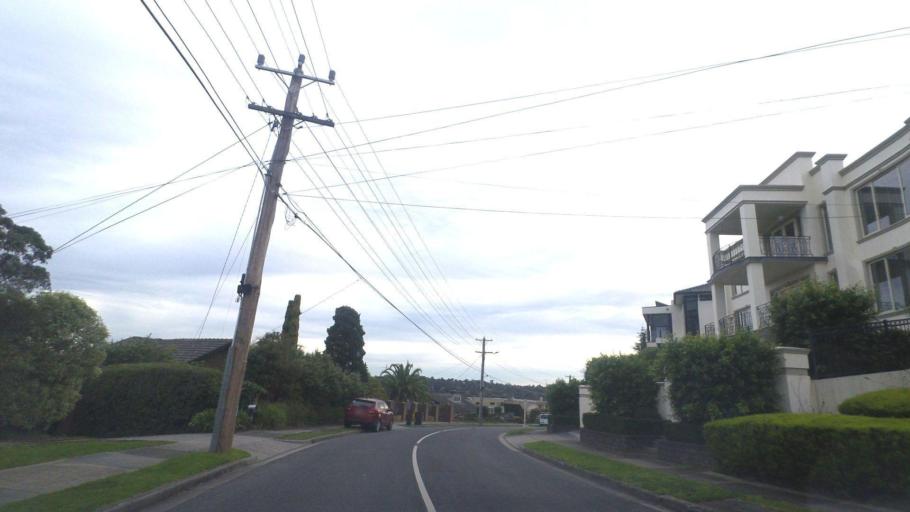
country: AU
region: Victoria
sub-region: Manningham
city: Bulleen
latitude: -37.7687
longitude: 145.0855
